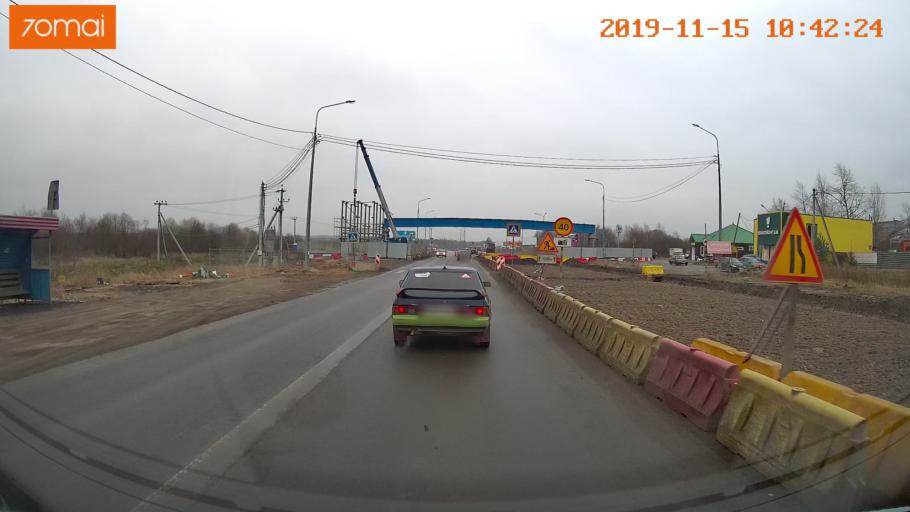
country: RU
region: Vologda
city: Sheksna
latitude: 59.2108
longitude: 38.5180
